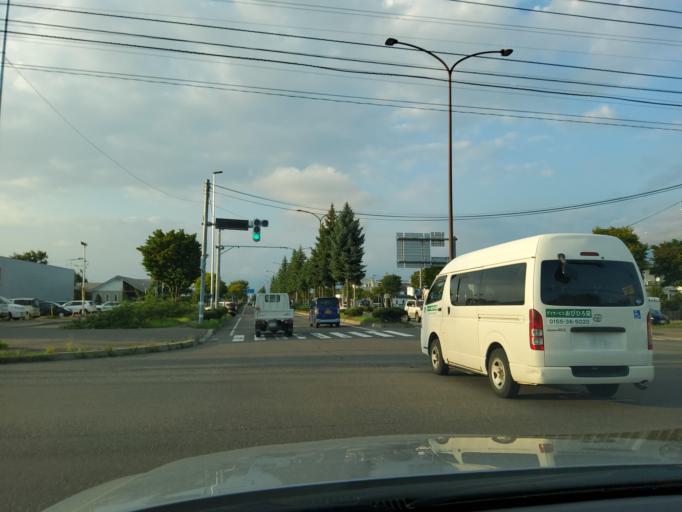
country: JP
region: Hokkaido
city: Obihiro
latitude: 42.9292
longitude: 143.1633
